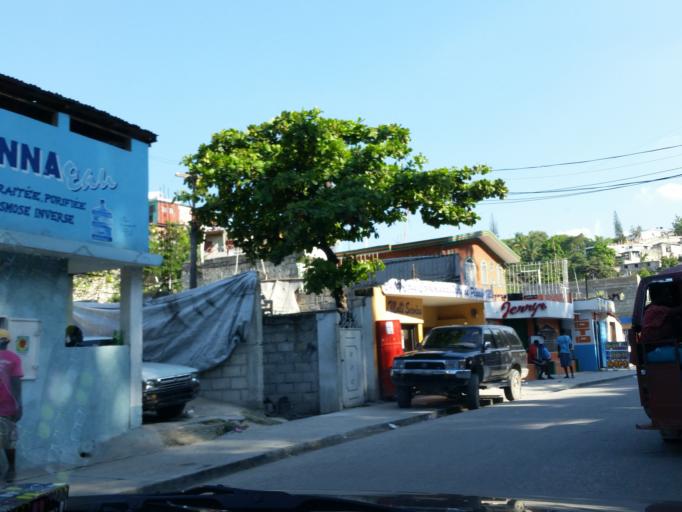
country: HT
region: Ouest
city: Petionville
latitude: 18.5162
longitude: -72.2800
